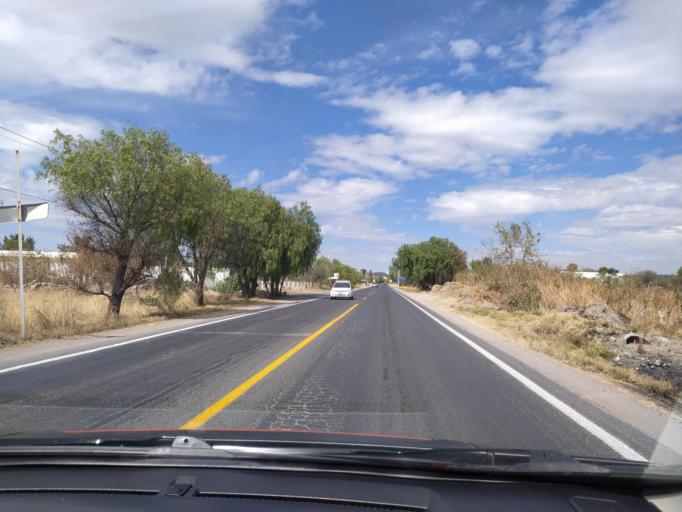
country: LA
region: Oudomxai
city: Muang La
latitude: 21.0224
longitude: 101.8260
